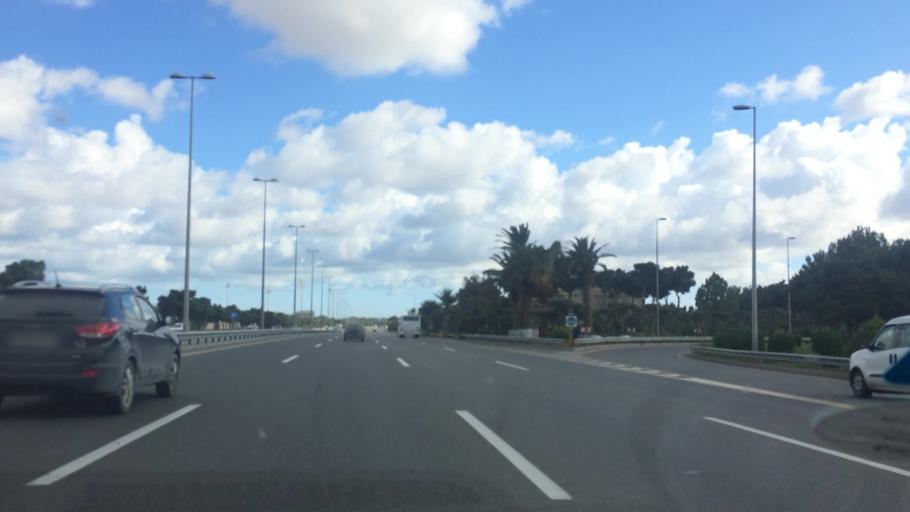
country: AZ
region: Baki
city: Biny Selo
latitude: 40.4595
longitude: 50.0762
